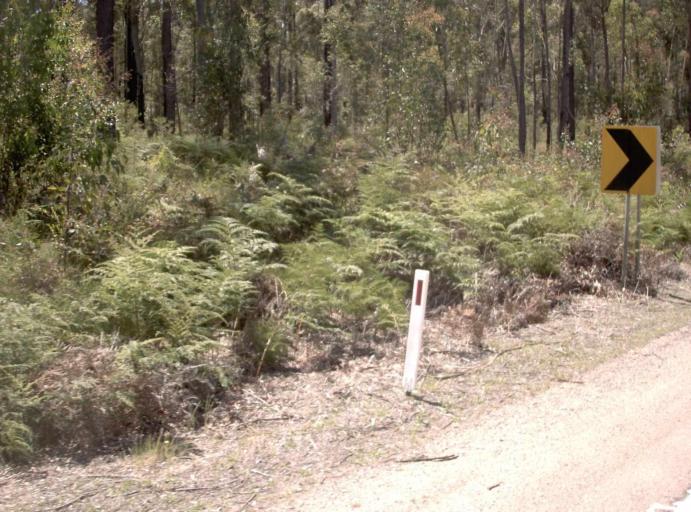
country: AU
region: Victoria
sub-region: East Gippsland
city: Lakes Entrance
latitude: -37.6880
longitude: 148.7509
